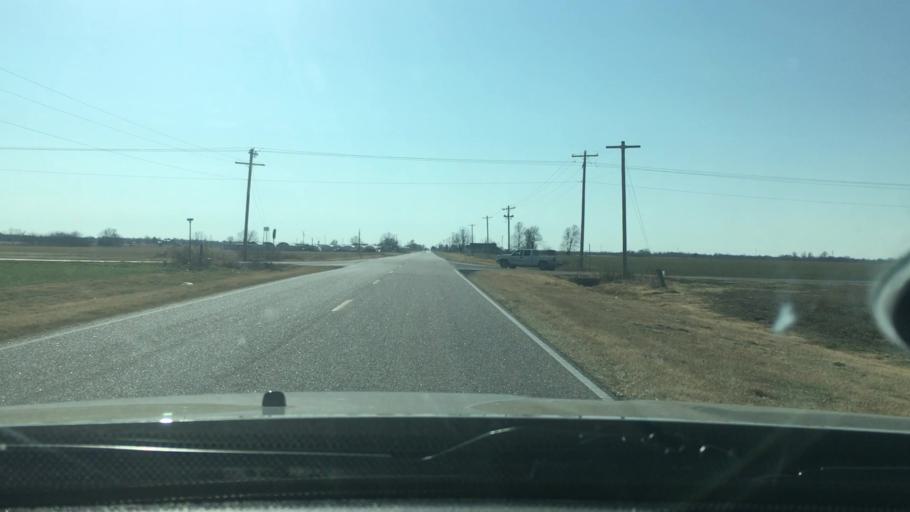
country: US
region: Oklahoma
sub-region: Garvin County
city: Stratford
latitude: 34.8262
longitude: -96.9677
